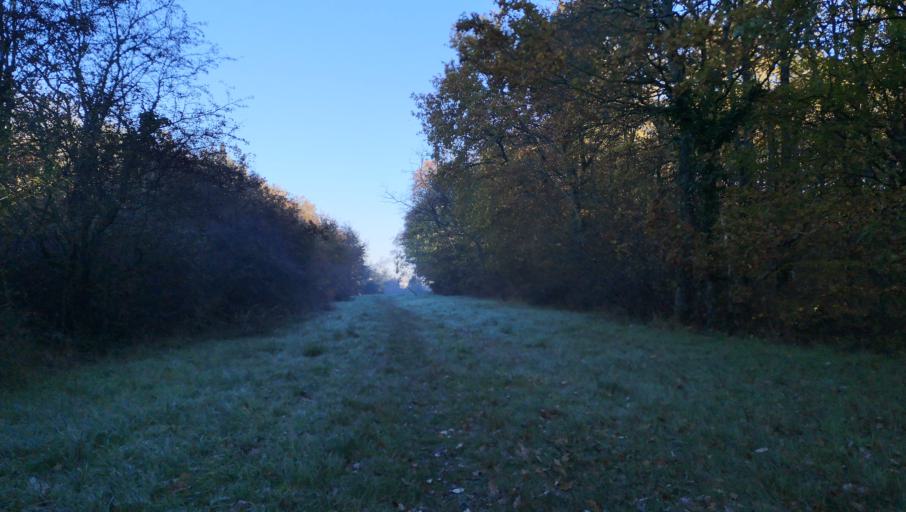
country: FR
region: Centre
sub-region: Departement du Loiret
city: Saran
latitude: 47.9453
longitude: 1.8590
